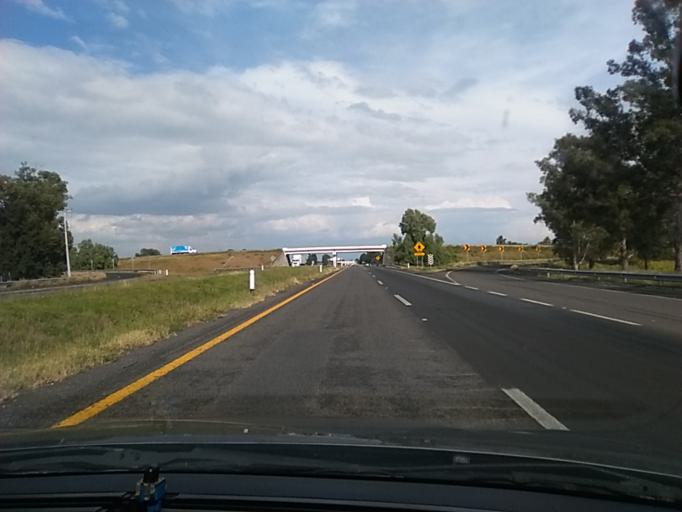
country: MX
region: Jalisco
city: La Barca
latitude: 20.3220
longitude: -102.5384
